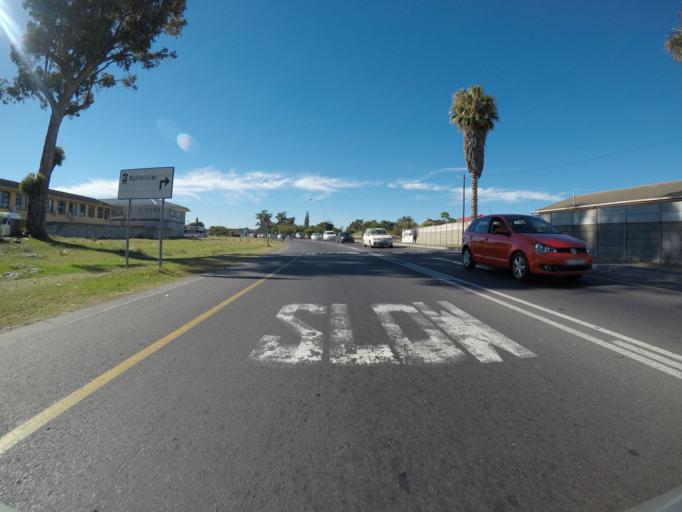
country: ZA
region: Western Cape
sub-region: City of Cape Town
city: Kraaifontein
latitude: -33.9361
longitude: 18.6768
